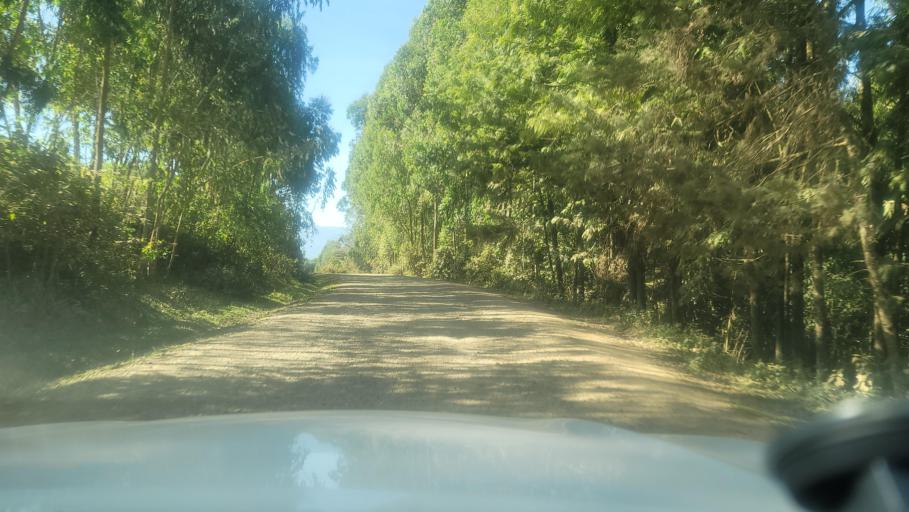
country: ET
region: Oromiya
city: Agaro
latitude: 7.8045
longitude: 36.5005
